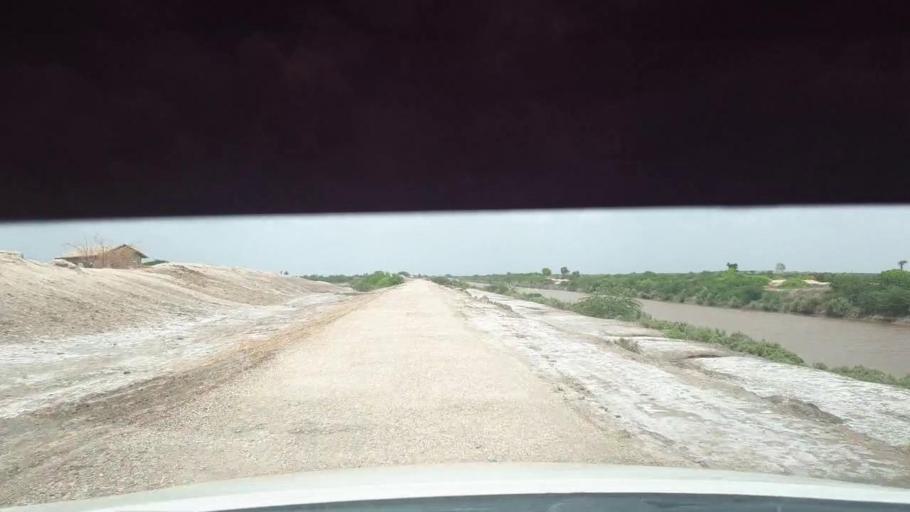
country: PK
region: Sindh
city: Kadhan
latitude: 24.5137
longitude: 69.1199
